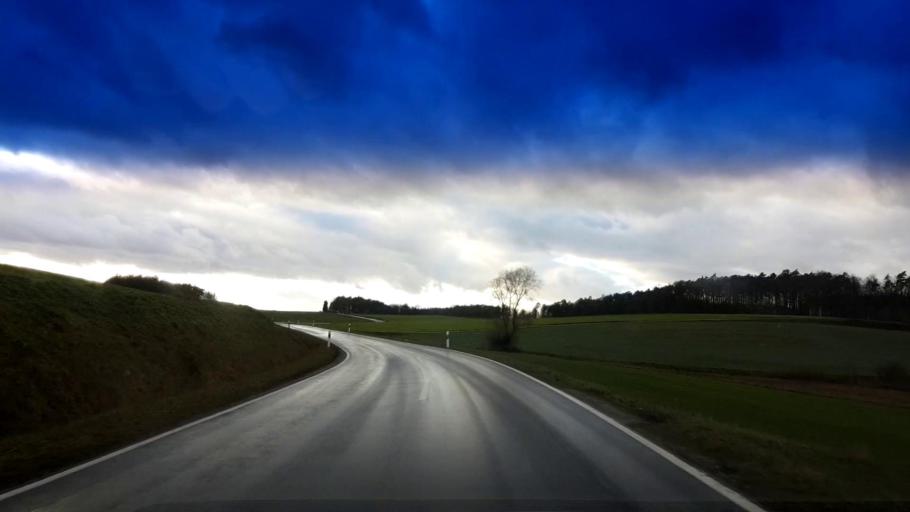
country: DE
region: Bavaria
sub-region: Upper Franconia
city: Lauter
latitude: 50.0030
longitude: 10.7728
